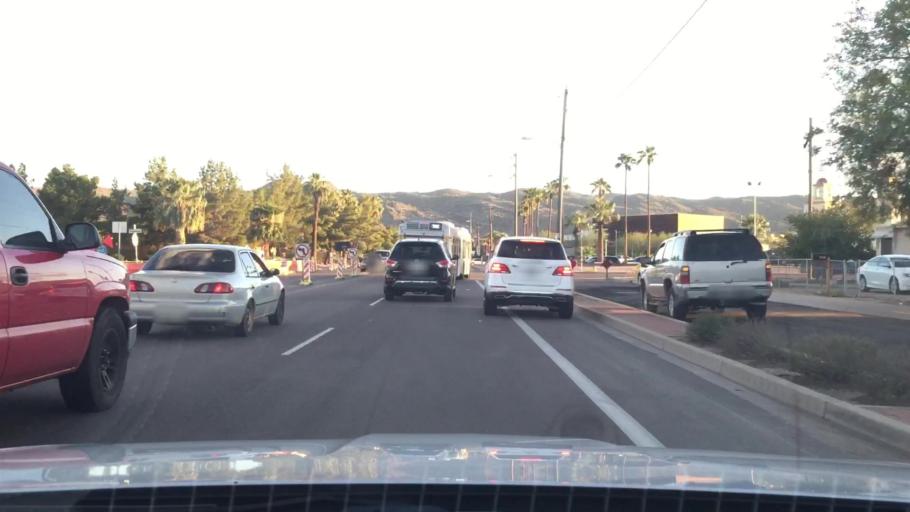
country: US
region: Arizona
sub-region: Maricopa County
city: Guadalupe
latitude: 33.3866
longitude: -112.0303
